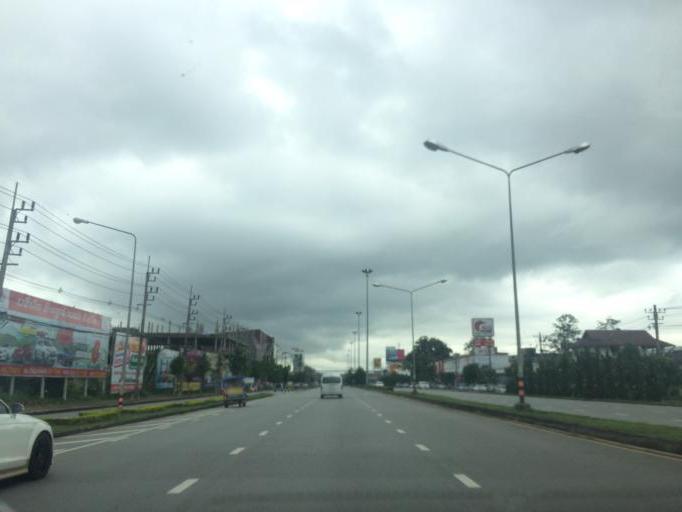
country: TH
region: Chiang Rai
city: Chiang Rai
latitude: 19.8831
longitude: 99.8344
